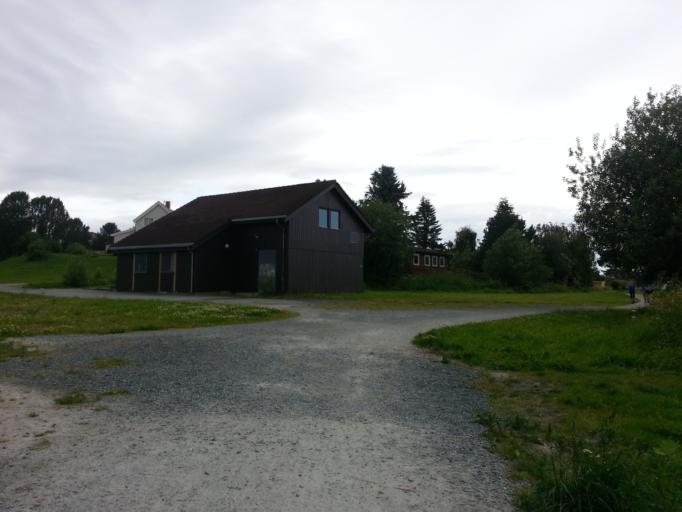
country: NO
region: Sor-Trondelag
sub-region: Trondheim
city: Trondheim
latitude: 63.4307
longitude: 10.5209
